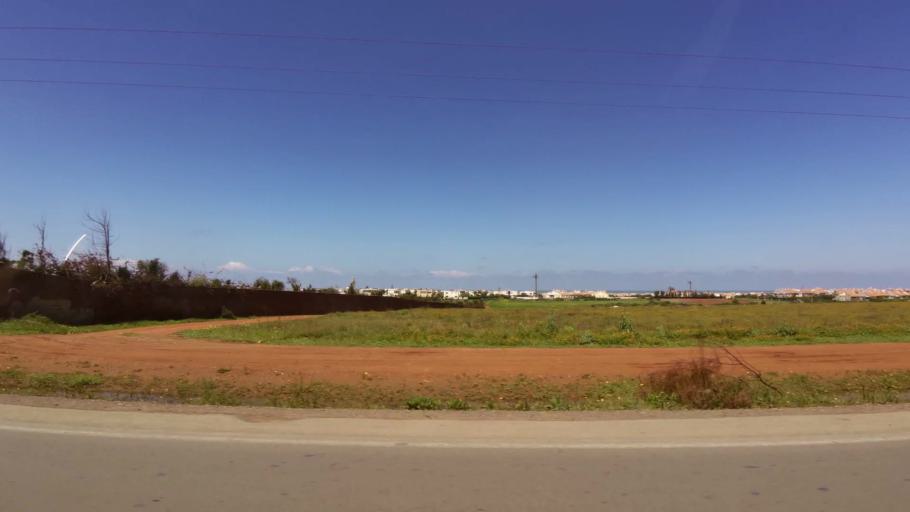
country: MA
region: Grand Casablanca
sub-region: Nouaceur
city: Dar Bouazza
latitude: 33.5293
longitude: -7.7754
